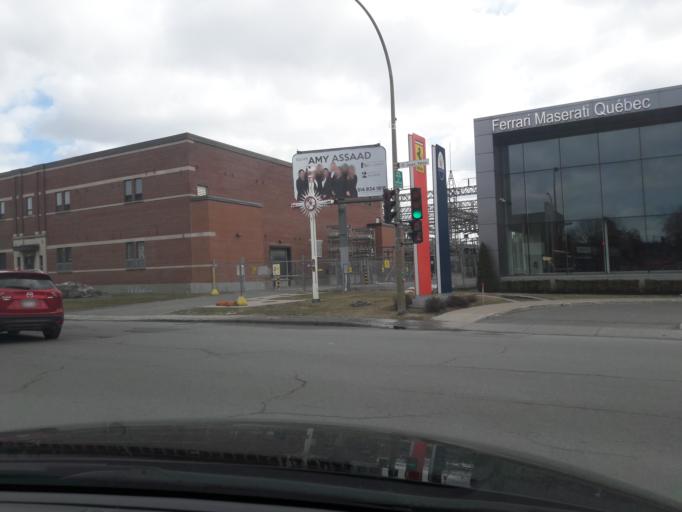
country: CA
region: Quebec
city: Mont-Royal
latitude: 45.5026
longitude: -73.6447
